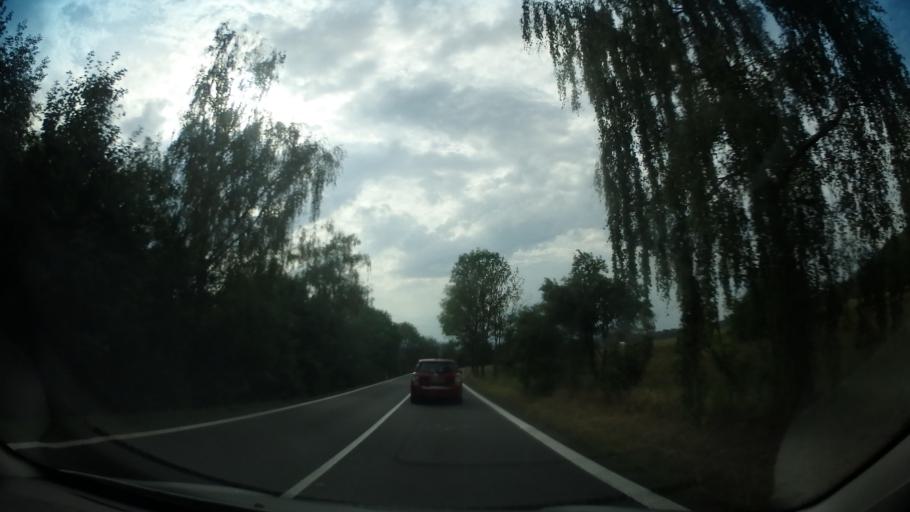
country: CZ
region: Pardubicky
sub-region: Okres Chrudim
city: Tremosnice
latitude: 49.8737
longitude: 15.5840
